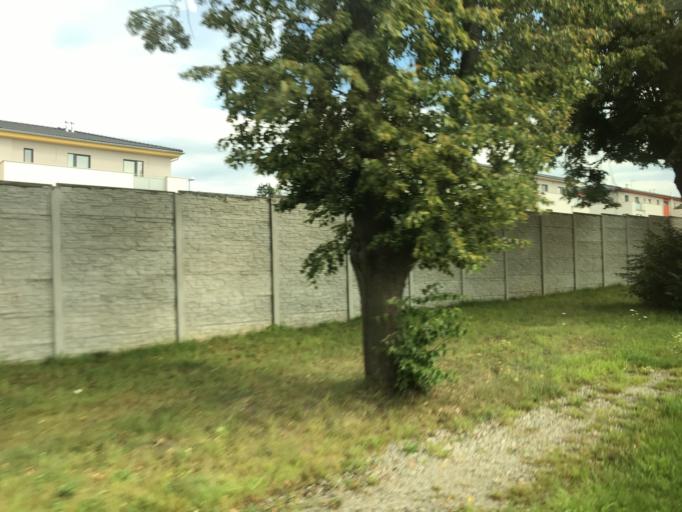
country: CZ
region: Jihocesky
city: Vcelna
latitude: 48.9290
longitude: 14.4572
